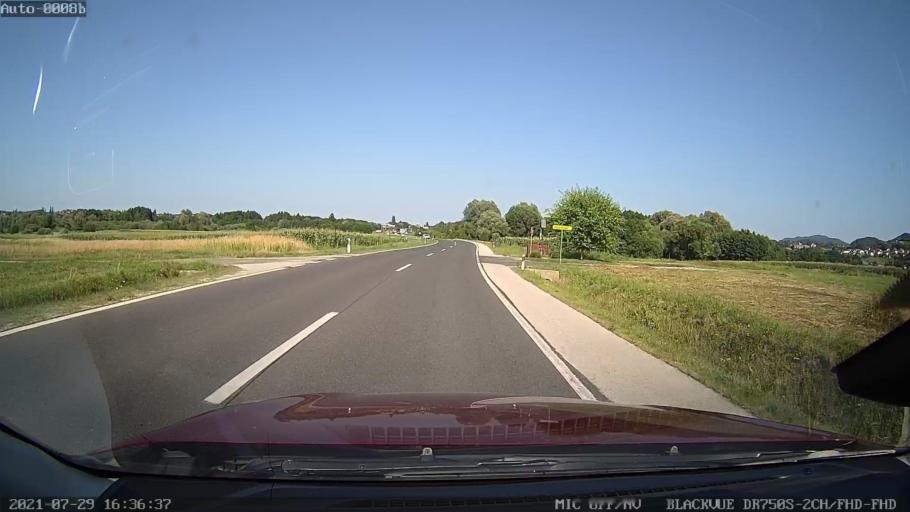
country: HR
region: Varazdinska
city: Ivanec
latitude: 46.2251
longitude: 16.0999
